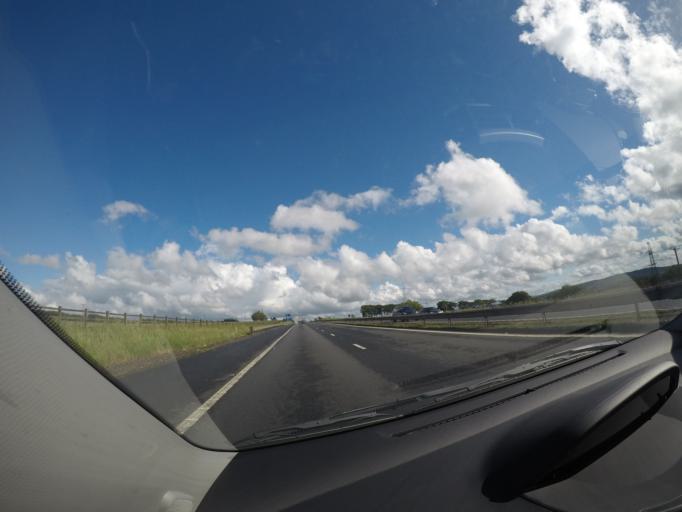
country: GB
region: Scotland
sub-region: South Lanarkshire
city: Lesmahagow
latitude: 55.6161
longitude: -3.8501
